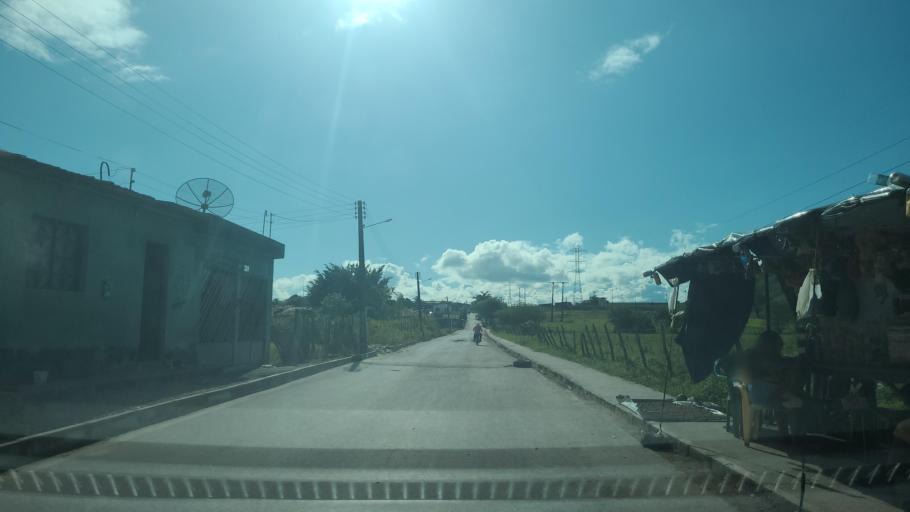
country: BR
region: Alagoas
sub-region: Uniao Dos Palmares
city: Uniao dos Palmares
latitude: -9.1577
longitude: -36.0188
